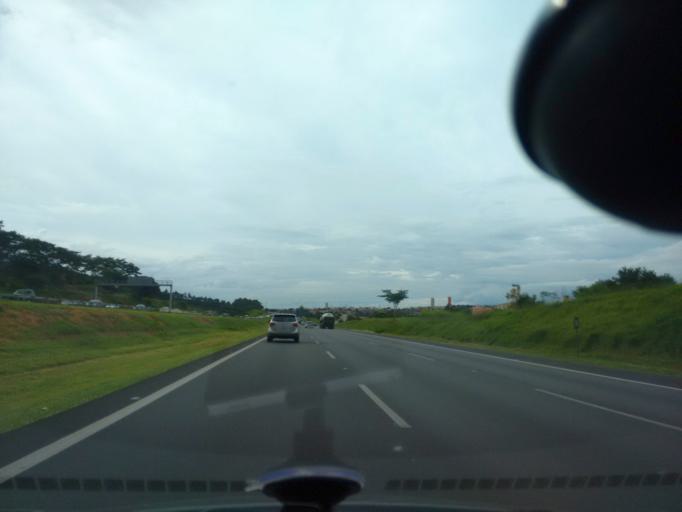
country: BR
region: Sao Paulo
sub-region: Campinas
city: Campinas
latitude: -22.9527
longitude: -47.1256
